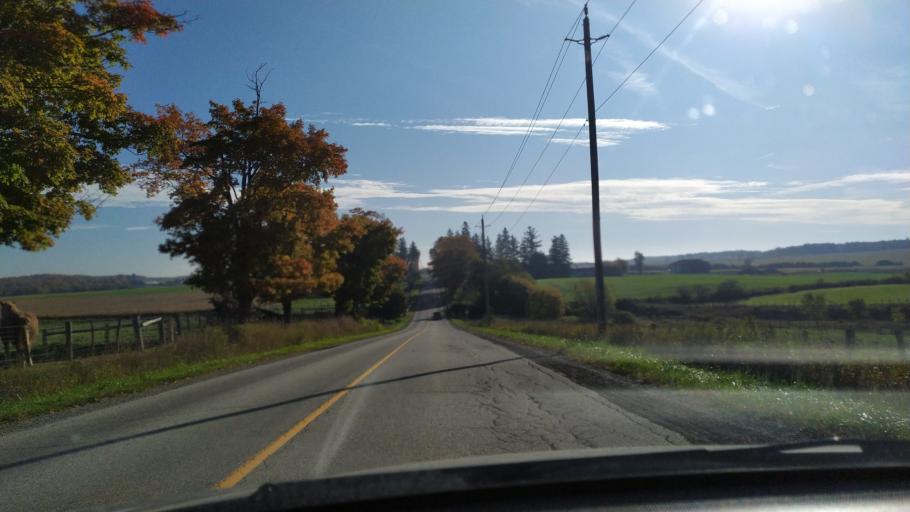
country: CA
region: Ontario
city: Waterloo
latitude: 43.4939
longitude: -80.7407
